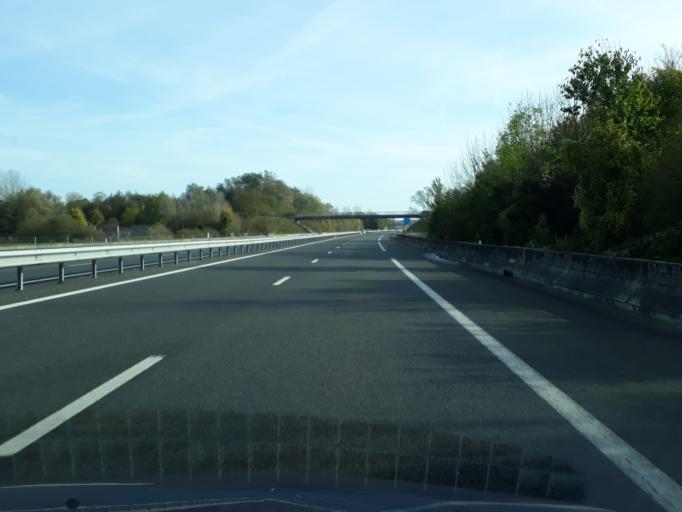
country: FR
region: Champagne-Ardenne
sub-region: Departement de l'Aube
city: Bucheres
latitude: 48.2223
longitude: 4.1207
